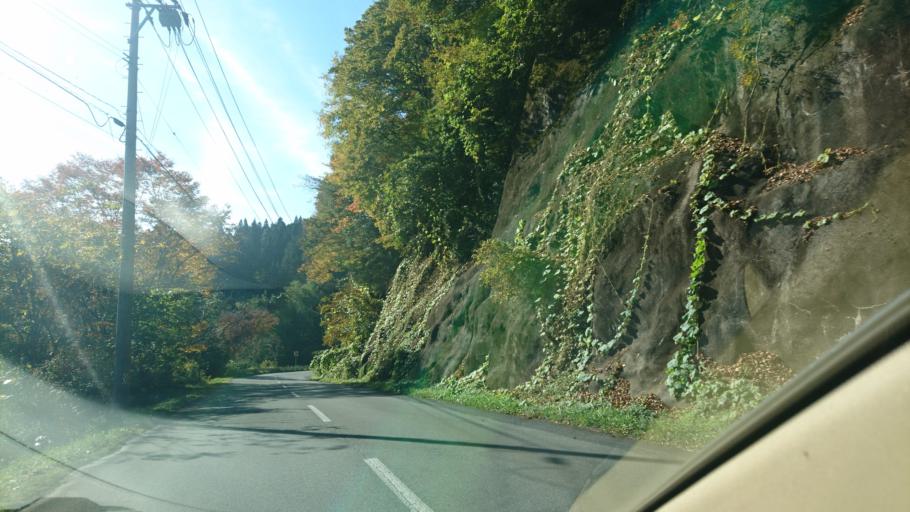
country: JP
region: Iwate
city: Ichinoseki
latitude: 39.0184
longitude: 141.3620
